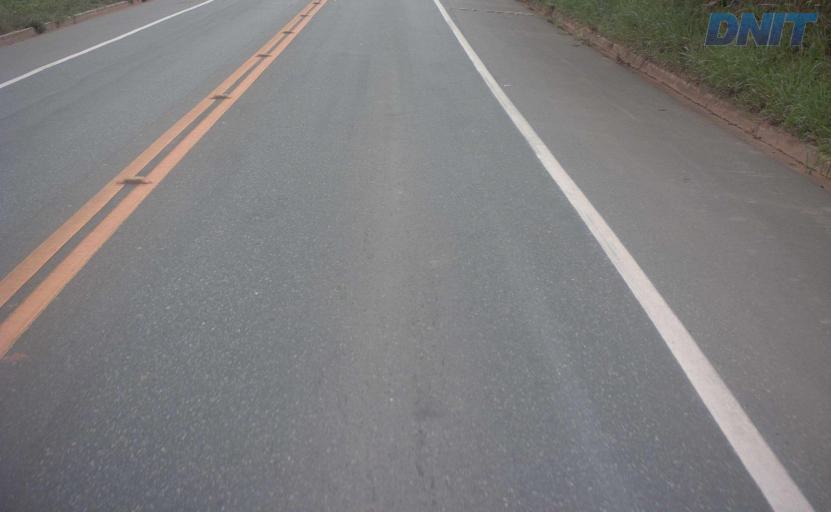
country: BR
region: Minas Gerais
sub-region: Nova Era
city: Nova Era
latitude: -19.7379
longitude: -43.0189
